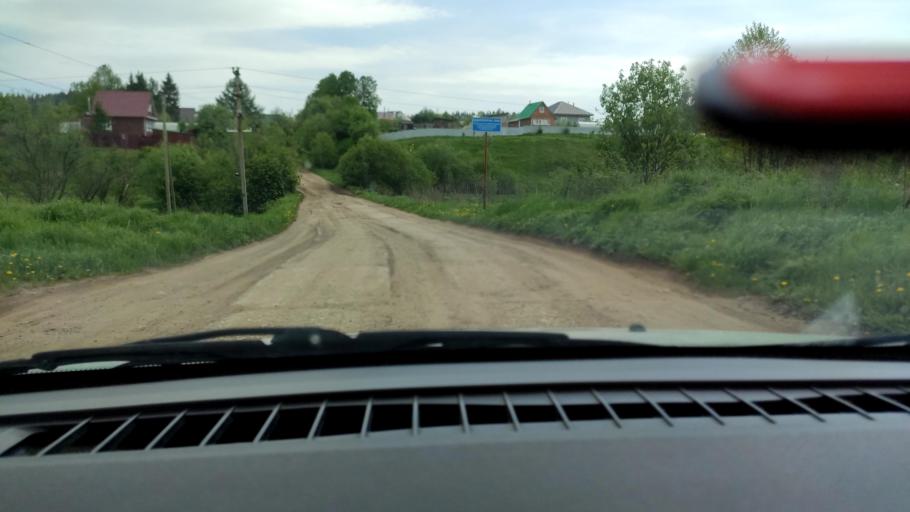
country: RU
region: Perm
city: Bershet'
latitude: 57.7279
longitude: 56.3803
